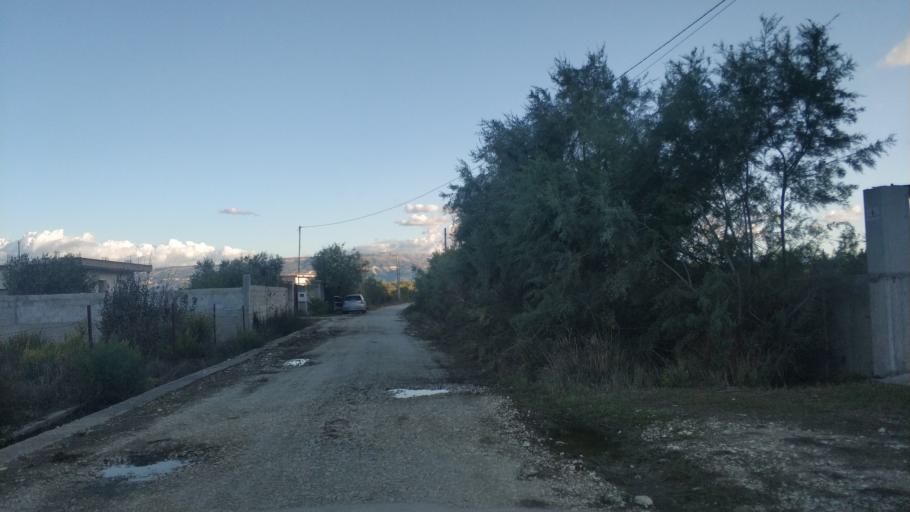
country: AL
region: Vlore
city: Vlore
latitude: 40.5096
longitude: 19.4222
